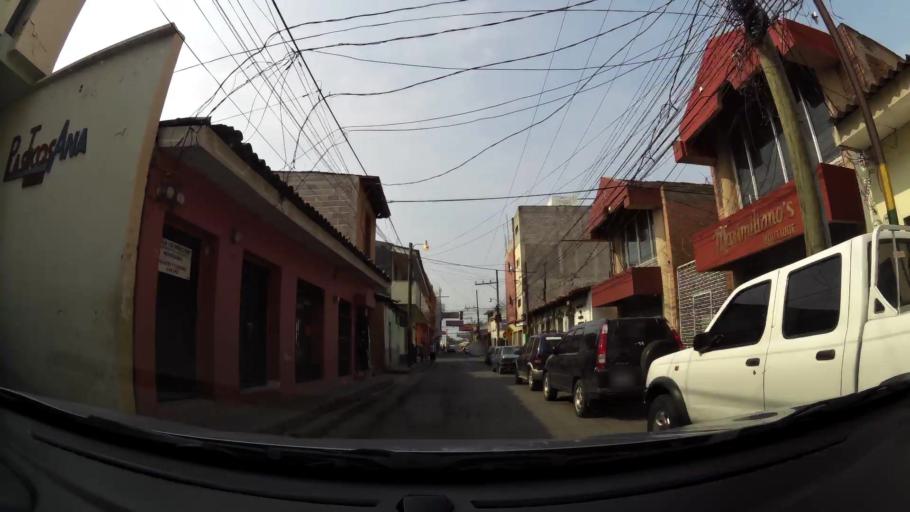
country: HN
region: Comayagua
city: Comayagua
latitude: 14.4567
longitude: -87.6415
